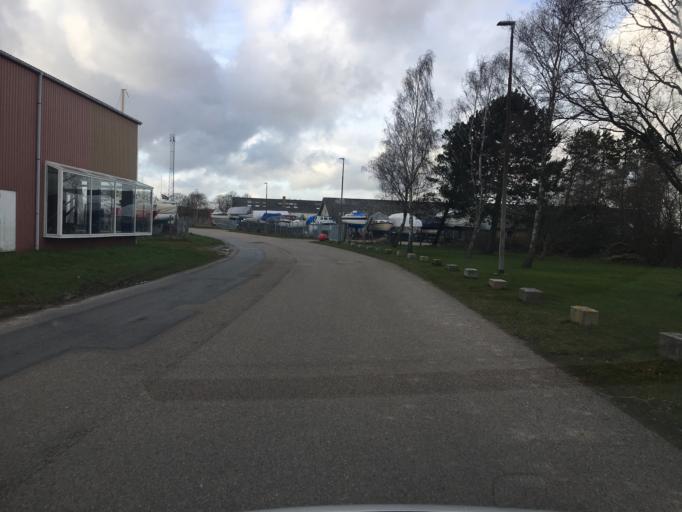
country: DK
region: South Denmark
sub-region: Sonderborg Kommune
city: Grasten
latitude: 54.9110
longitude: 9.5994
